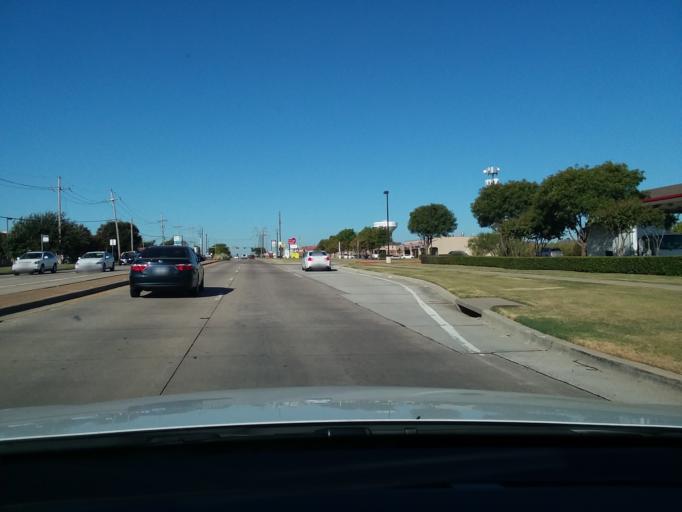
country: US
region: Texas
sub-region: Denton County
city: Highland Village
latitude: 33.0714
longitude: -97.0240
